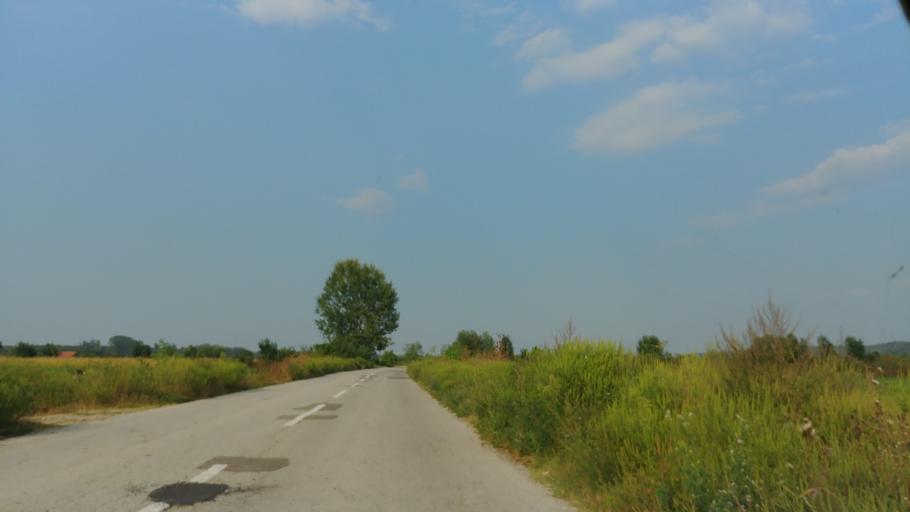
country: BA
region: Republika Srpska
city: Lopare
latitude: 44.7341
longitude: 18.8487
